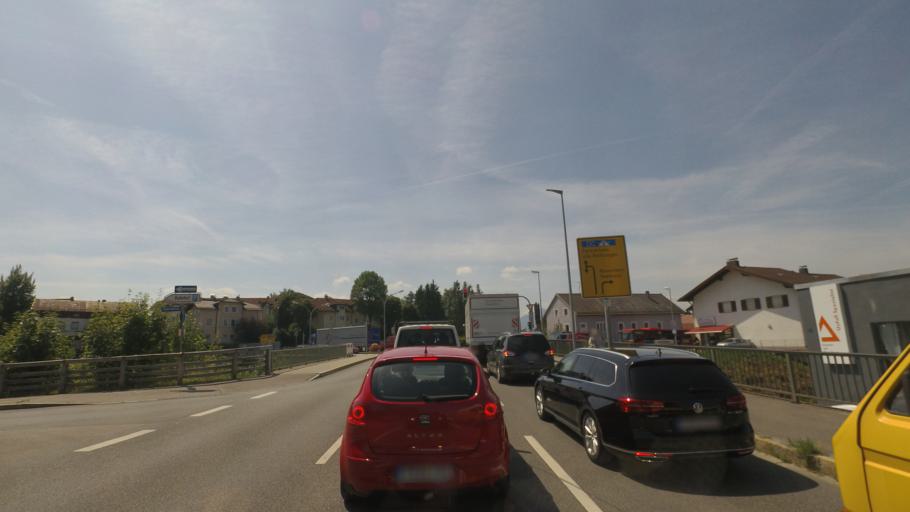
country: DE
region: Bavaria
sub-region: Upper Bavaria
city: Traunstein
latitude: 47.8675
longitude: 12.6324
